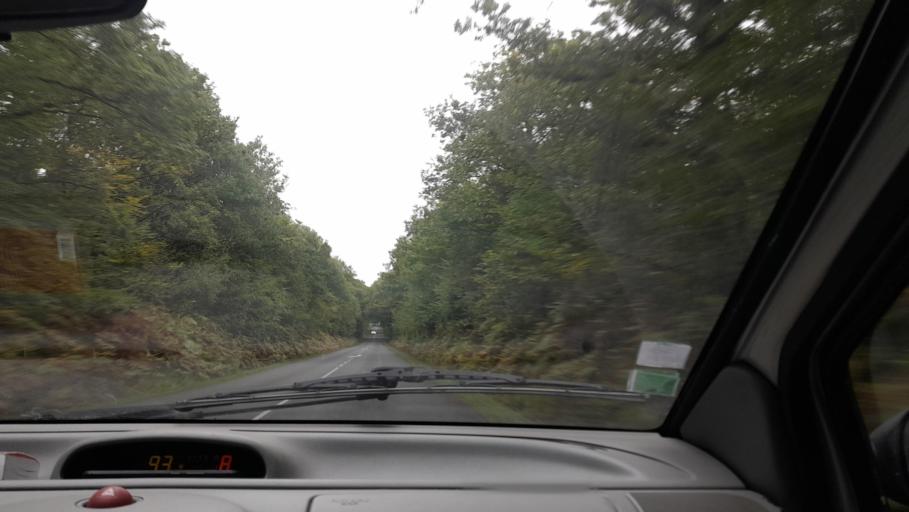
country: FR
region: Pays de la Loire
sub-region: Departement de Maine-et-Loire
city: Pouance
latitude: 47.7041
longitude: -1.1794
